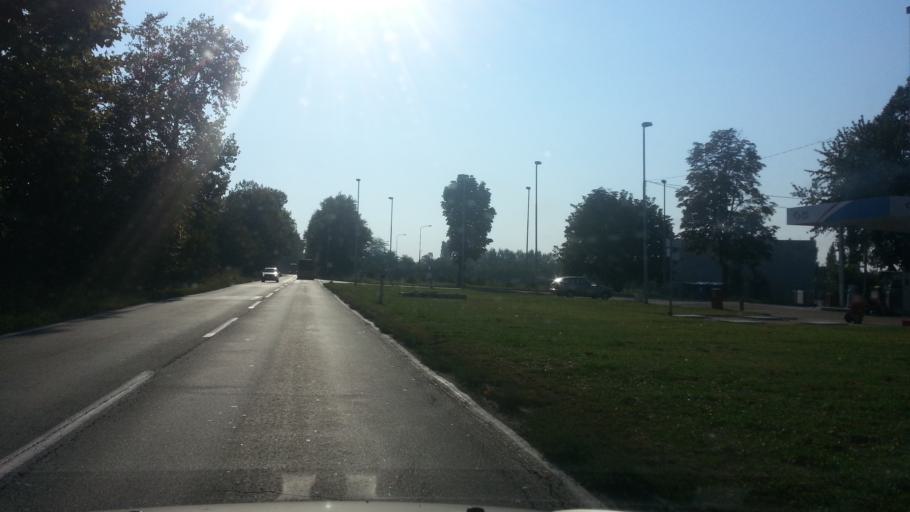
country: RS
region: Central Serbia
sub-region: Belgrade
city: Zemun
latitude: 44.8710
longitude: 20.3505
